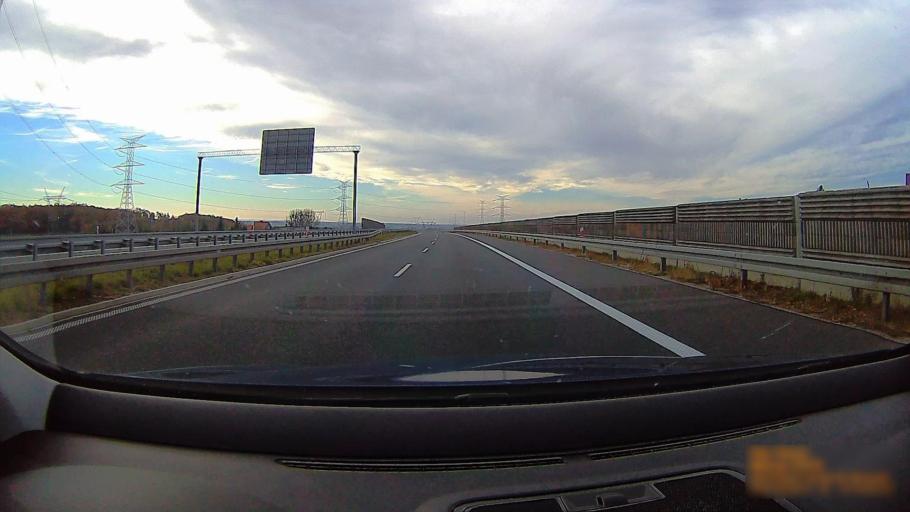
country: PL
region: Greater Poland Voivodeship
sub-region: Powiat ostrowski
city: Przygodzice
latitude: 51.6224
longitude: 17.8626
